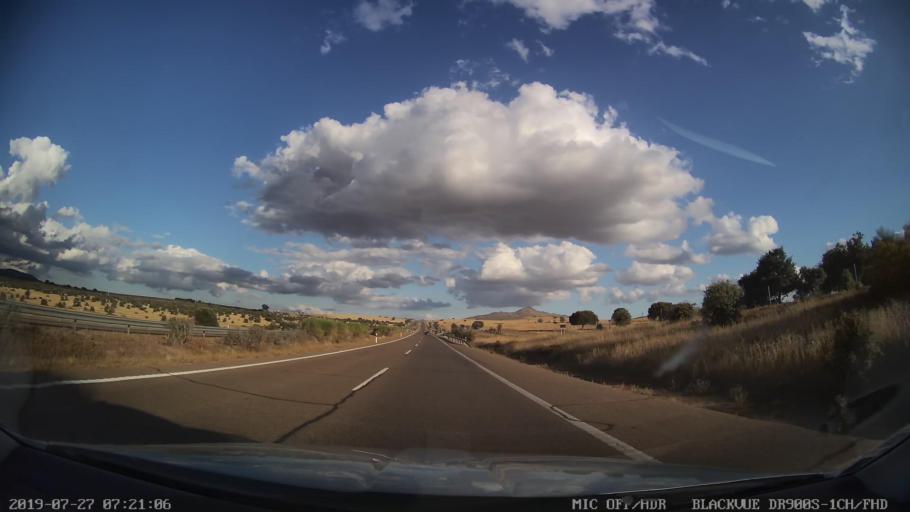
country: ES
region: Extremadura
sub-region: Provincia de Caceres
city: Santa Cruz de la Sierra
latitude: 39.3683
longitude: -5.8750
